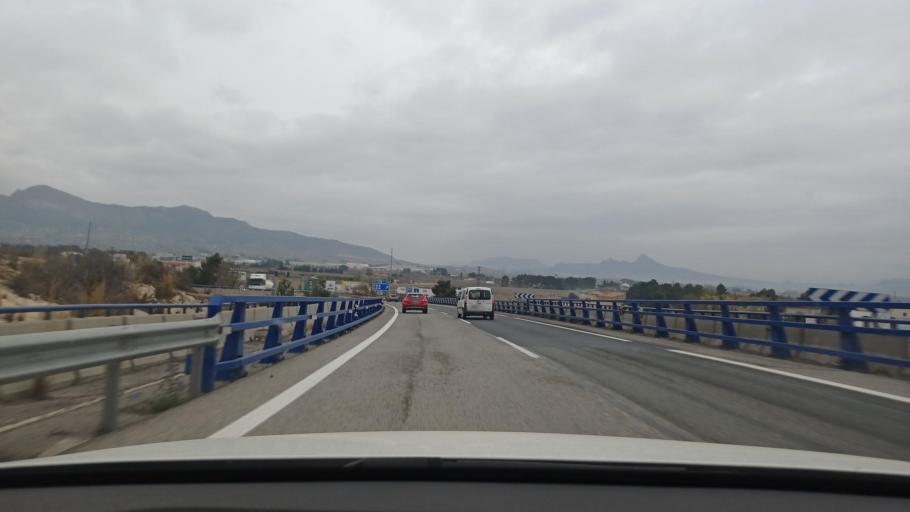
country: ES
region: Valencia
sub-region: Provincia de Alicante
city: Villena
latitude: 38.6298
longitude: -0.8587
